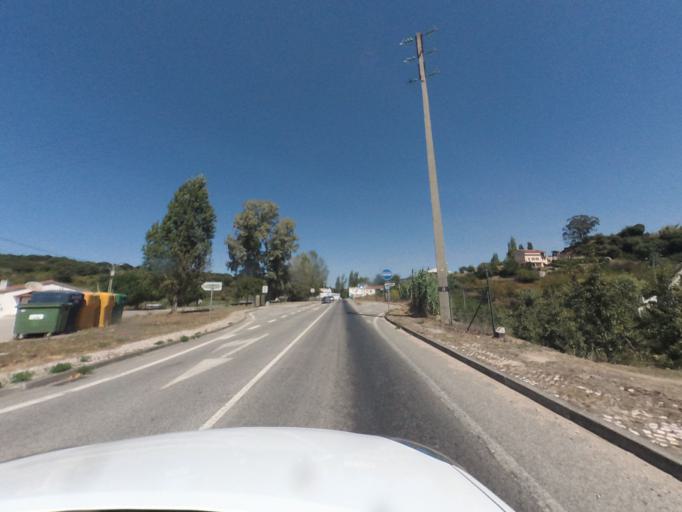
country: PT
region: Leiria
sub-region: Alcobaca
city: Alcobaca
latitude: 39.5255
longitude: -9.0002
